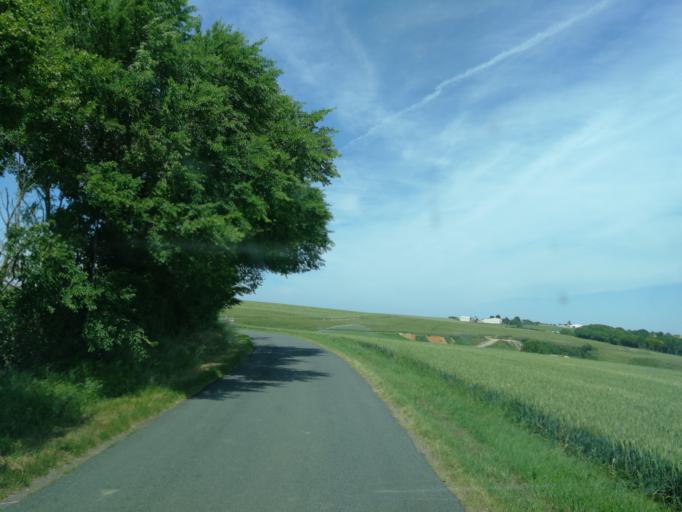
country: FR
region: Pays de la Loire
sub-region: Departement de la Vendee
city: Le Langon
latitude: 46.4335
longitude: -0.8894
